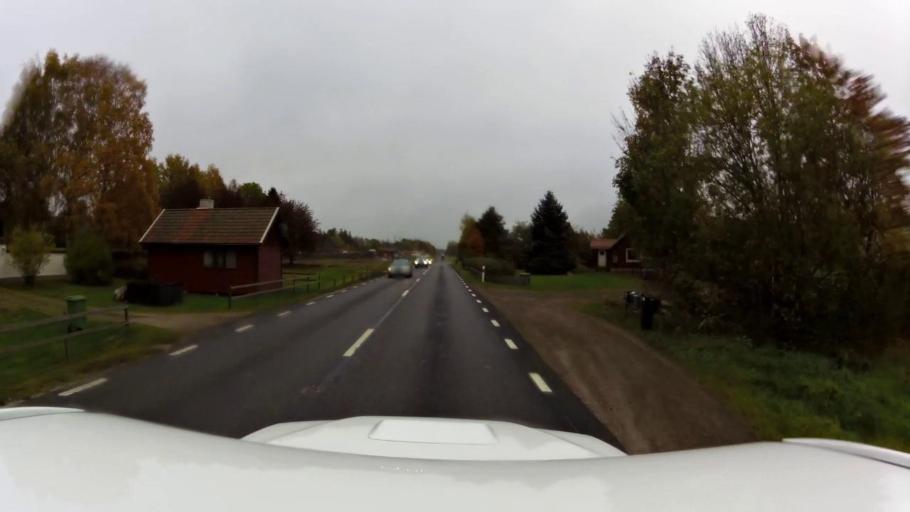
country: SE
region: OEstergoetland
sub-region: Linkopings Kommun
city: Linghem
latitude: 58.3830
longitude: 15.7902
